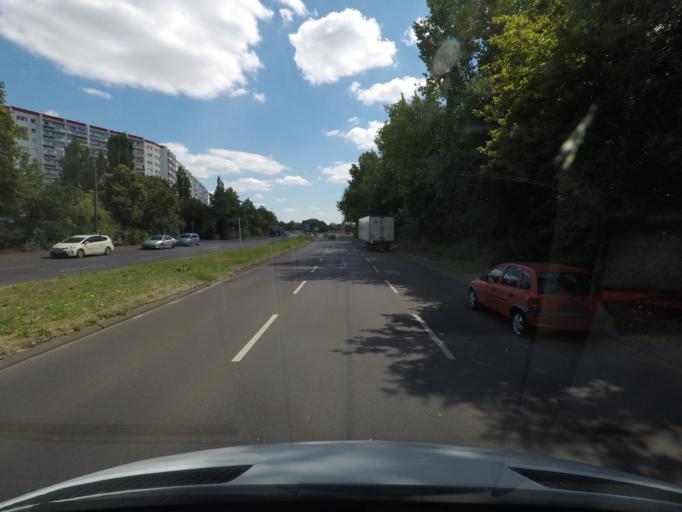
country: DE
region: Berlin
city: Biesdorf
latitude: 52.5230
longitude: 13.5395
